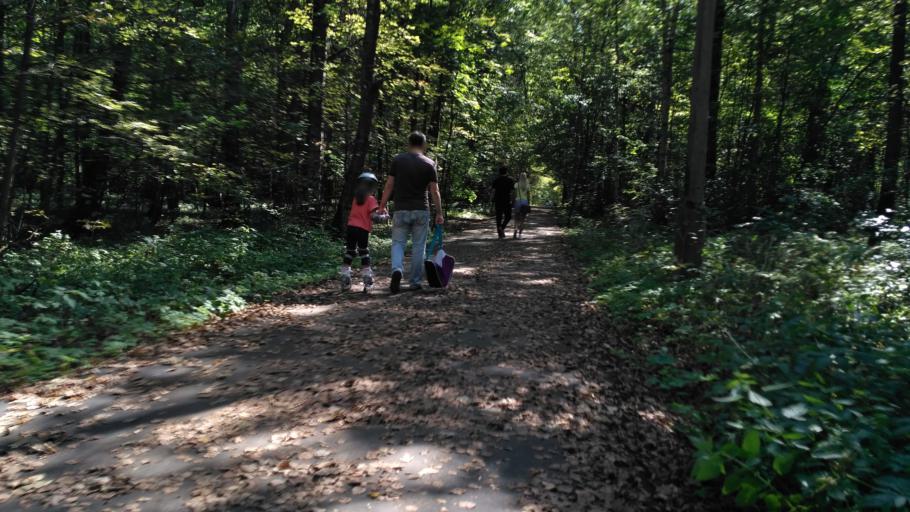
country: RU
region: Moscow
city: Ryazanskiy
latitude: 55.7748
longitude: 37.7591
